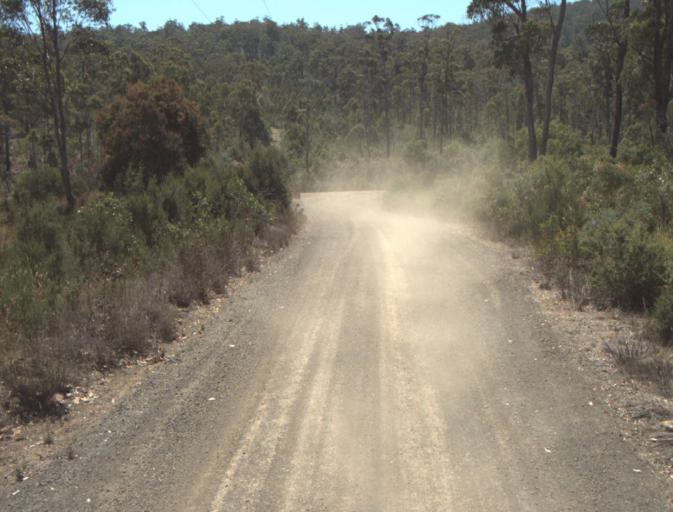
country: AU
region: Tasmania
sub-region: Launceston
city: Mayfield
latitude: -41.2728
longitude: 147.0995
